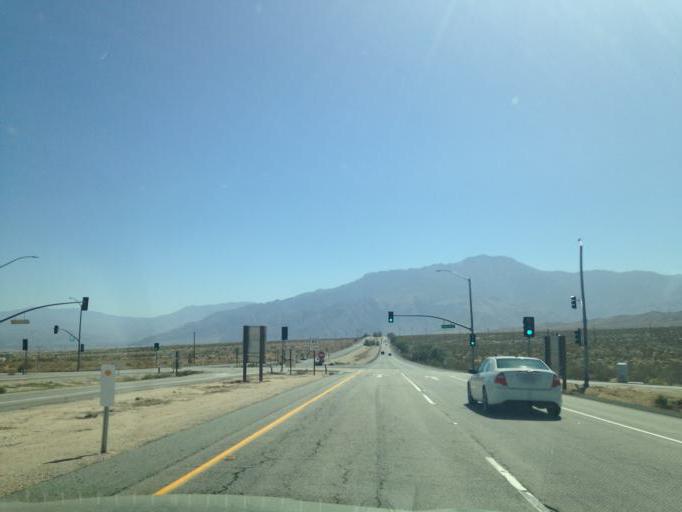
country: US
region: California
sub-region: San Bernardino County
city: Morongo Valley
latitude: 34.0056
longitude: -116.5764
